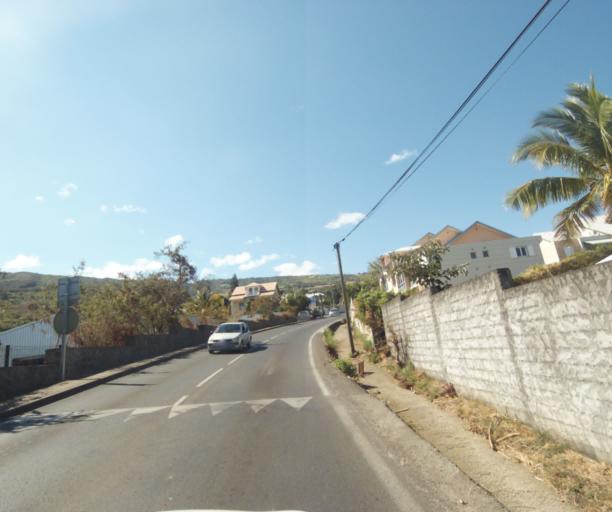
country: RE
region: Reunion
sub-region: Reunion
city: La Possession
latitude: -20.9814
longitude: 55.3339
